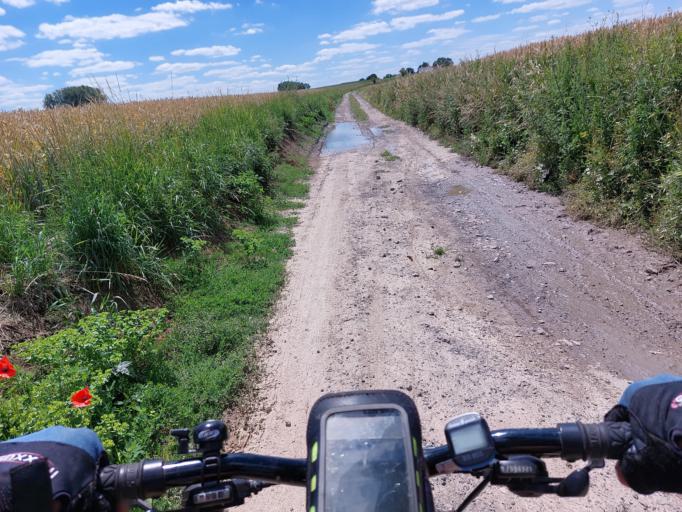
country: BE
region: Wallonia
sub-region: Province du Hainaut
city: Silly
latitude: 50.6145
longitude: 3.9025
